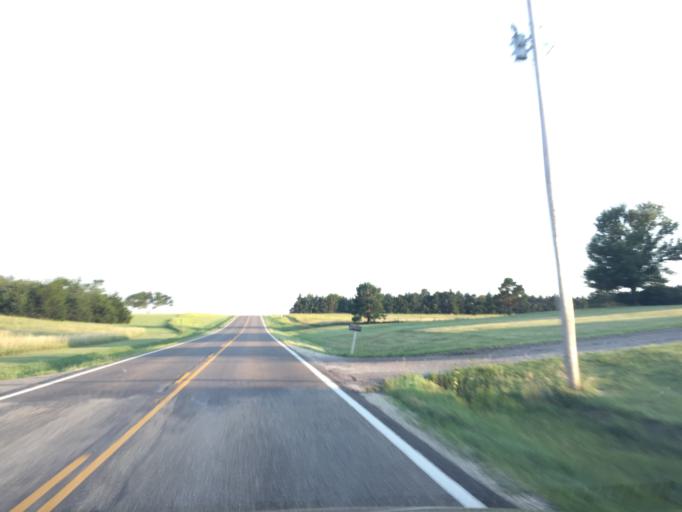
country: US
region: Kansas
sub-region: Ellsworth County
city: Ellsworth
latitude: 38.7641
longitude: -98.2251
